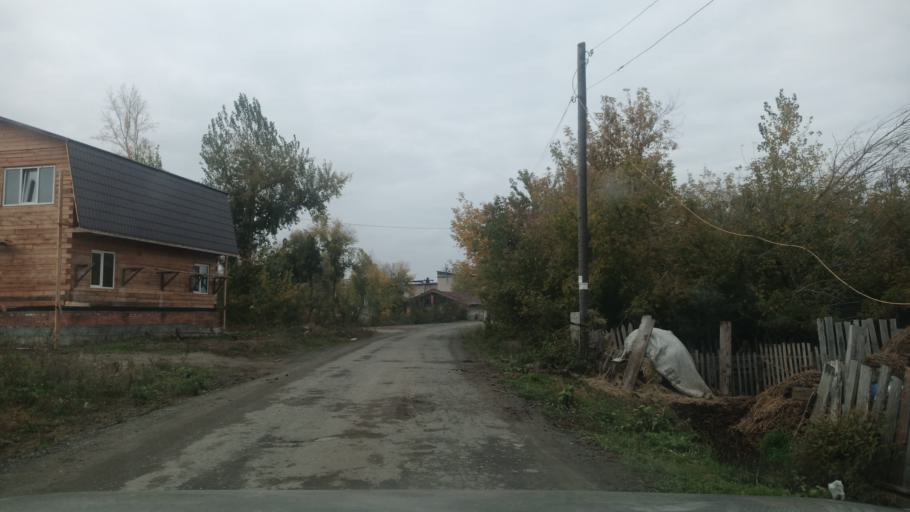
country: RU
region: Altai Krai
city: Zaton
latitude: 53.2984
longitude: 83.8037
